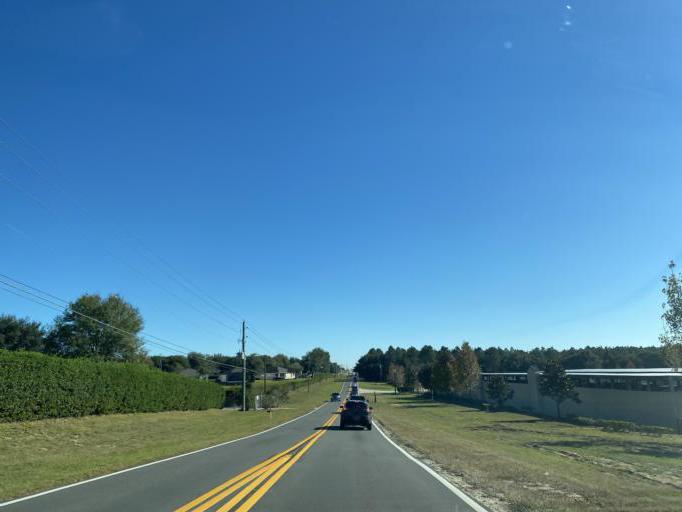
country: US
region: Florida
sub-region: Lake County
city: Clermont
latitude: 28.4998
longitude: -81.7139
